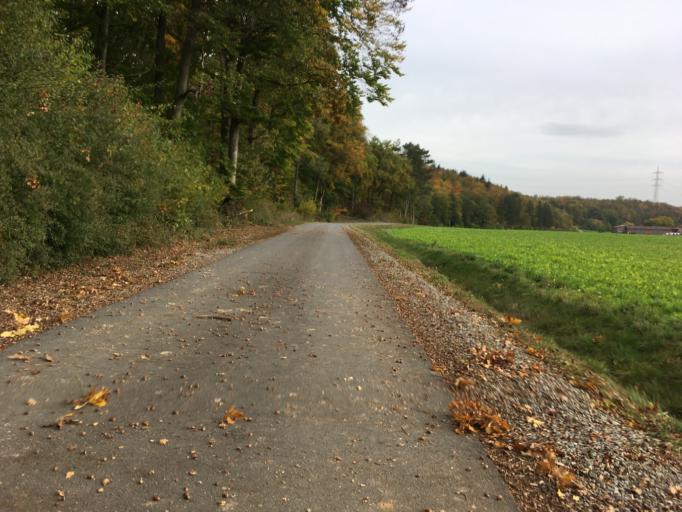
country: DE
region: Baden-Wuerttemberg
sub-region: Karlsruhe Region
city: Buchen
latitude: 49.4939
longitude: 9.3376
